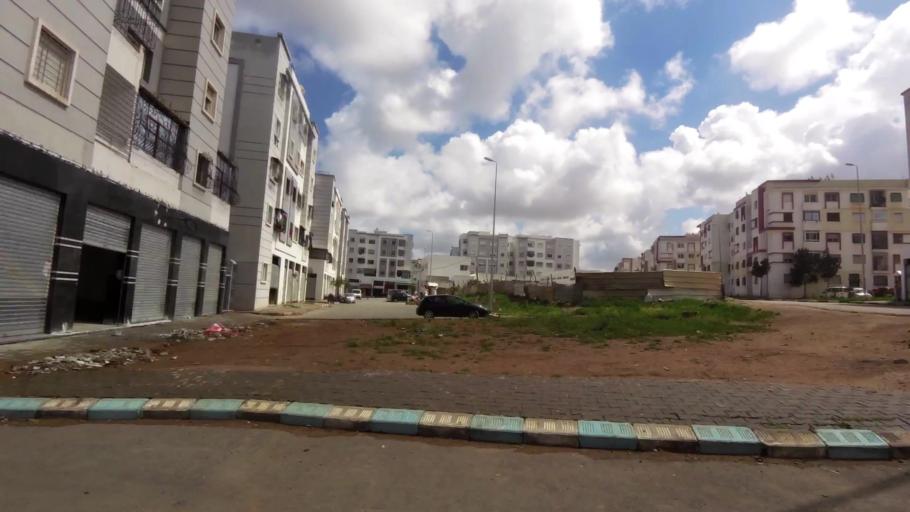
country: MA
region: Grand Casablanca
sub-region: Nouaceur
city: Dar Bouazza
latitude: 33.5329
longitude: -7.7192
